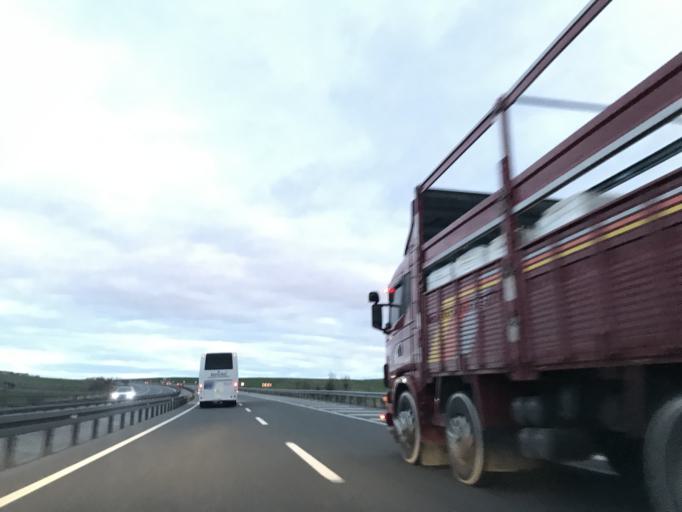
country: TR
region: Ankara
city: Altpinar
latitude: 39.2976
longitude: 32.9481
